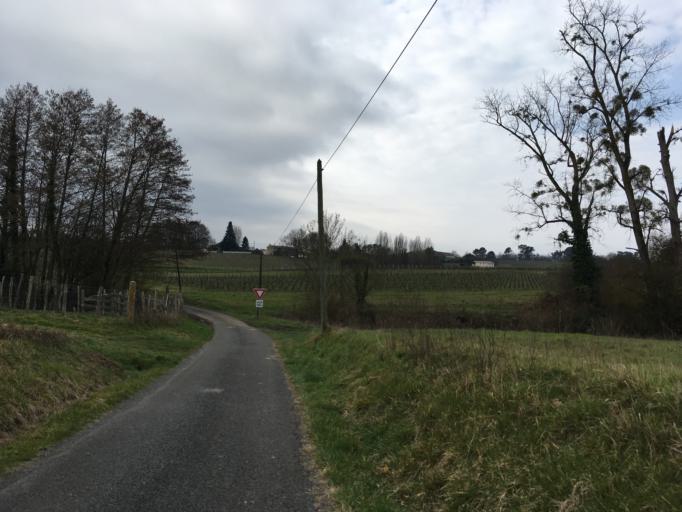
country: FR
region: Poitou-Charentes
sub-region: Departement de la Charente-Maritime
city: Mirambeau
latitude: 45.3320
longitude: -0.5871
